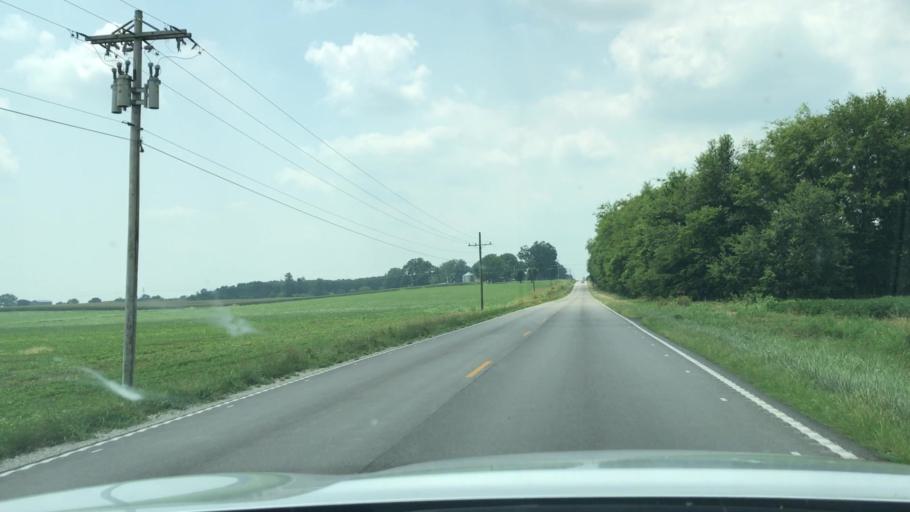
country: US
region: Kentucky
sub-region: Todd County
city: Guthrie
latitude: 36.6816
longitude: -87.1447
